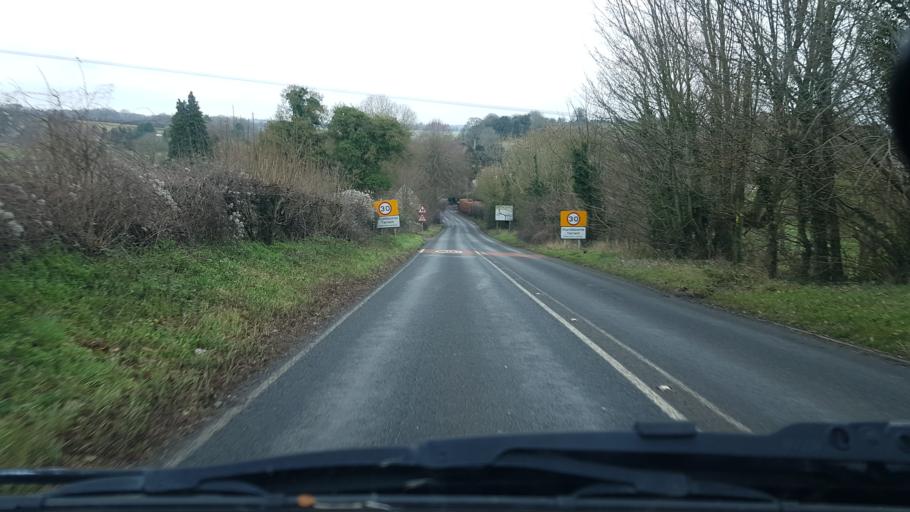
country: GB
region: England
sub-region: Hampshire
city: Andover
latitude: 51.2744
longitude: -1.4566
